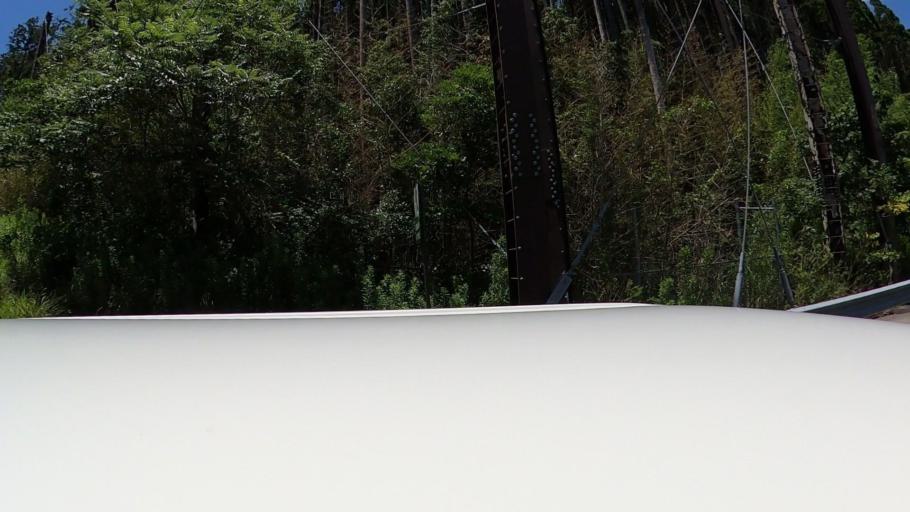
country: JP
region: Miyazaki
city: Nobeoka
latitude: 32.3867
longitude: 131.6215
